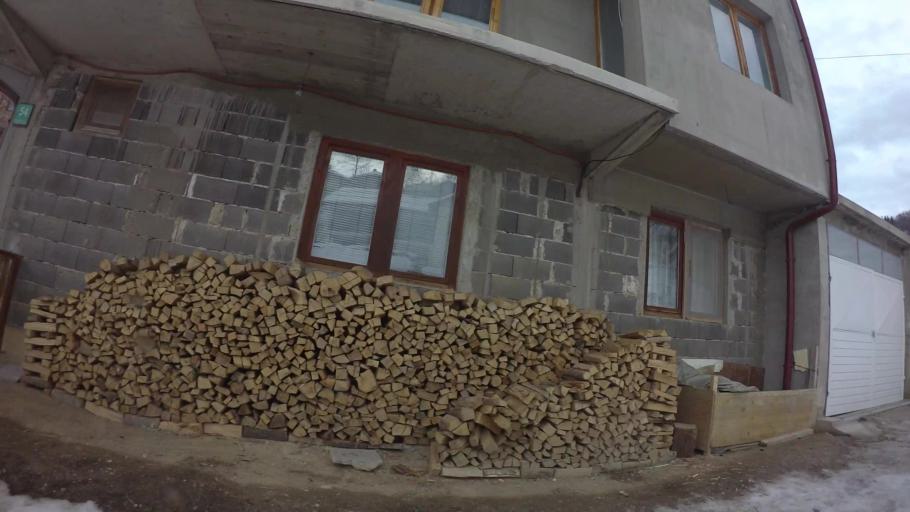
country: BA
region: Federation of Bosnia and Herzegovina
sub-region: Kanton Sarajevo
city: Sarajevo
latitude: 43.8597
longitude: 18.3336
